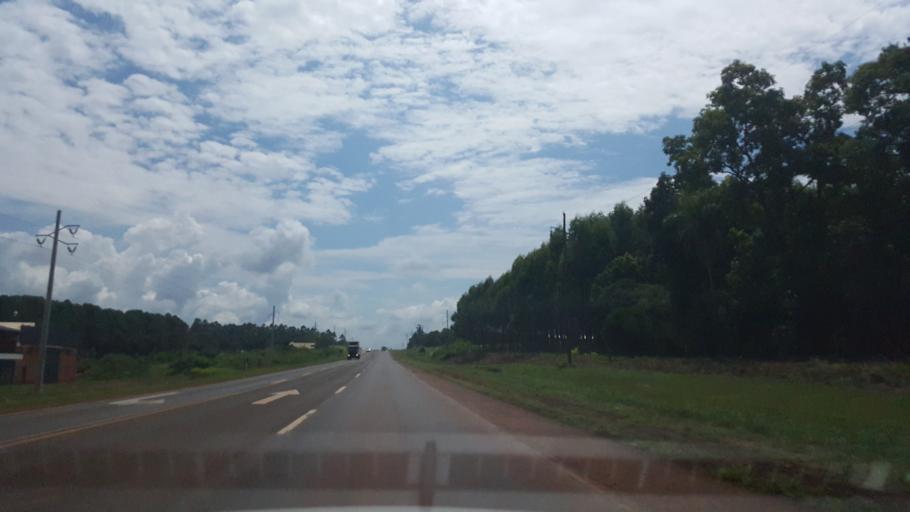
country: AR
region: Misiones
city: Puerto Rico
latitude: -26.8484
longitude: -55.0432
